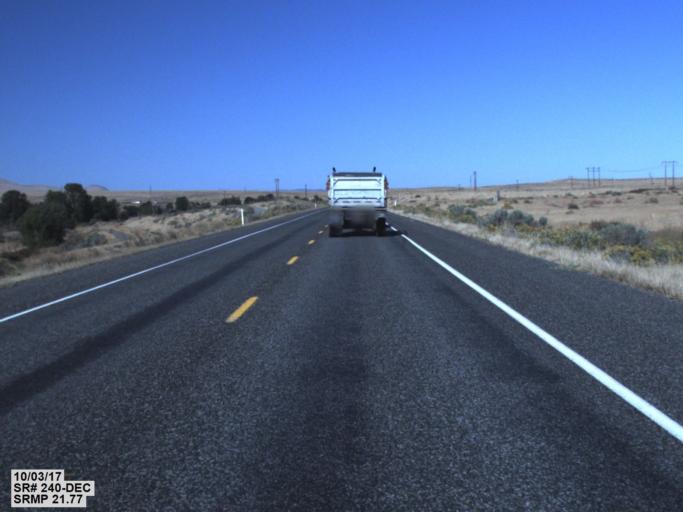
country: US
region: Washington
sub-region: Benton County
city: West Richland
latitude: 46.3717
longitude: -119.4016
